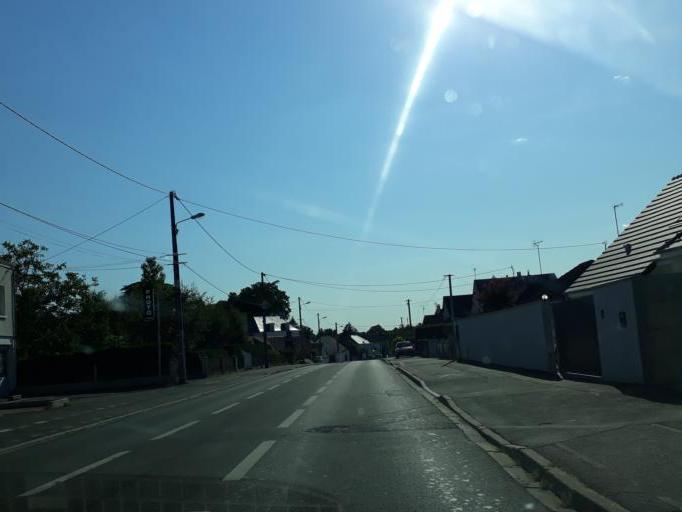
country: FR
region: Centre
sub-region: Departement du Loiret
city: Saint-Jean-de-Braye
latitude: 47.9165
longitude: 1.9758
